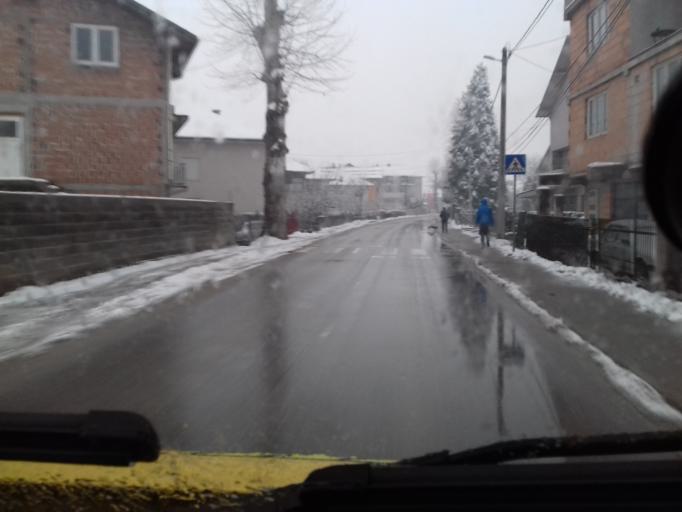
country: BA
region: Federation of Bosnia and Herzegovina
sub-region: Kanton Sarajevo
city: Sarajevo
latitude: 43.8179
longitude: 18.3270
